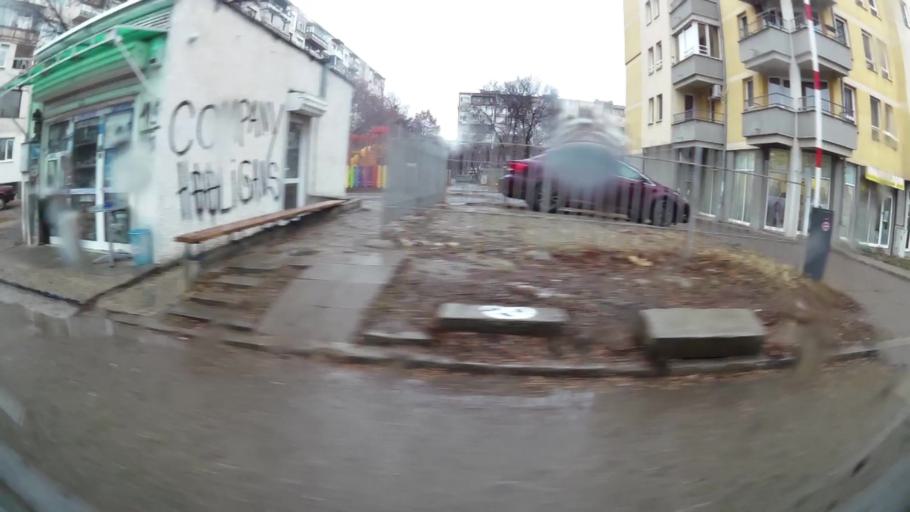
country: BG
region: Sofia-Capital
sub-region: Stolichna Obshtina
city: Sofia
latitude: 42.6534
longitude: 23.3690
